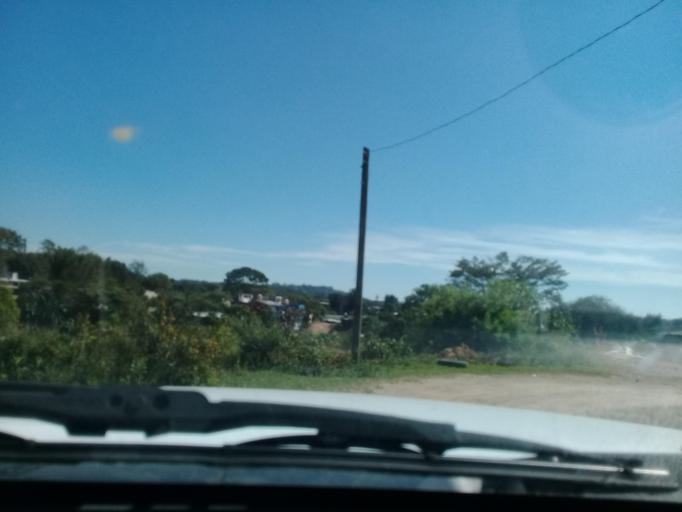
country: MX
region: Veracruz
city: El Castillo
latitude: 19.5508
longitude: -96.8556
